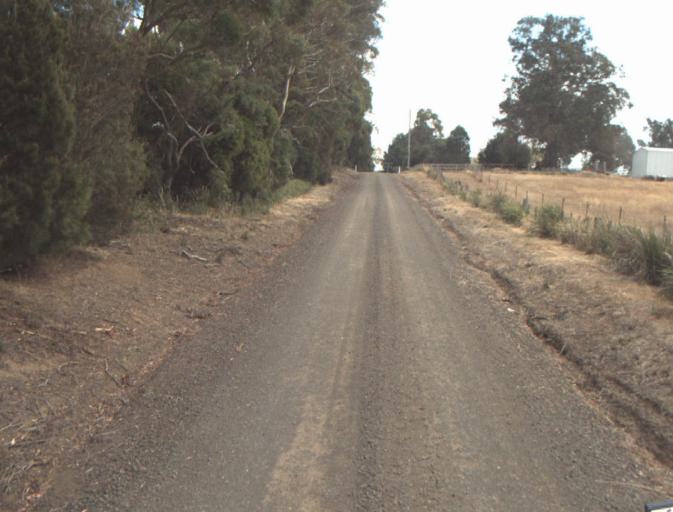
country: AU
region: Tasmania
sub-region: Launceston
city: Mayfield
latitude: -41.2787
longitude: 147.0452
